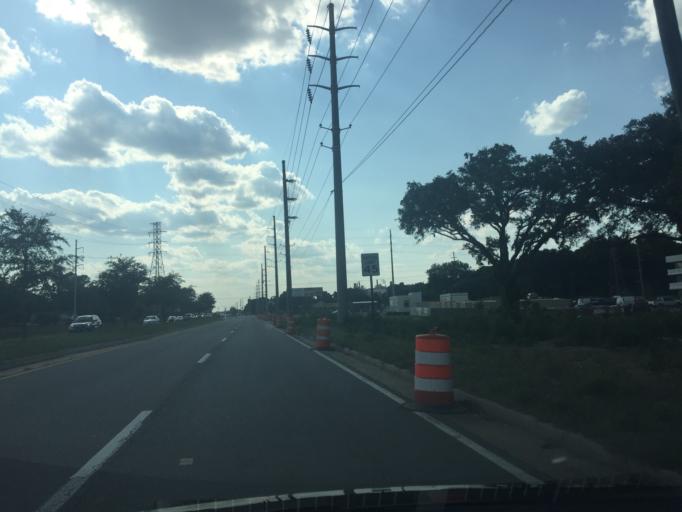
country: US
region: Georgia
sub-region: Chatham County
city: Thunderbolt
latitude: 32.0689
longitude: -81.0528
